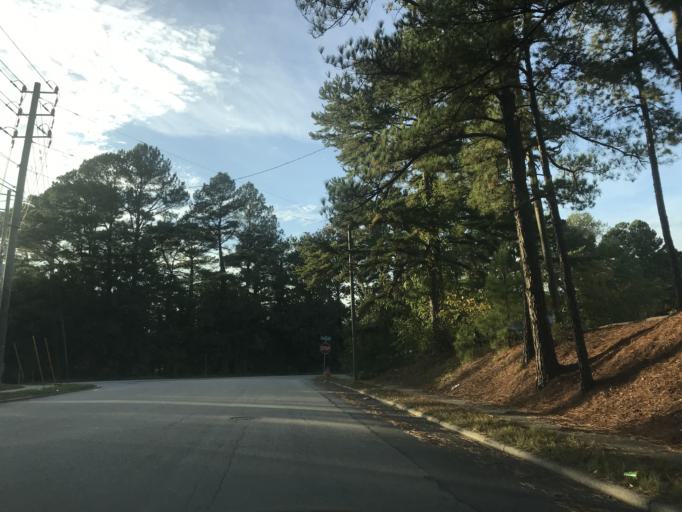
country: US
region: North Carolina
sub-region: Wake County
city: Raleigh
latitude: 35.8257
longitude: -78.6133
